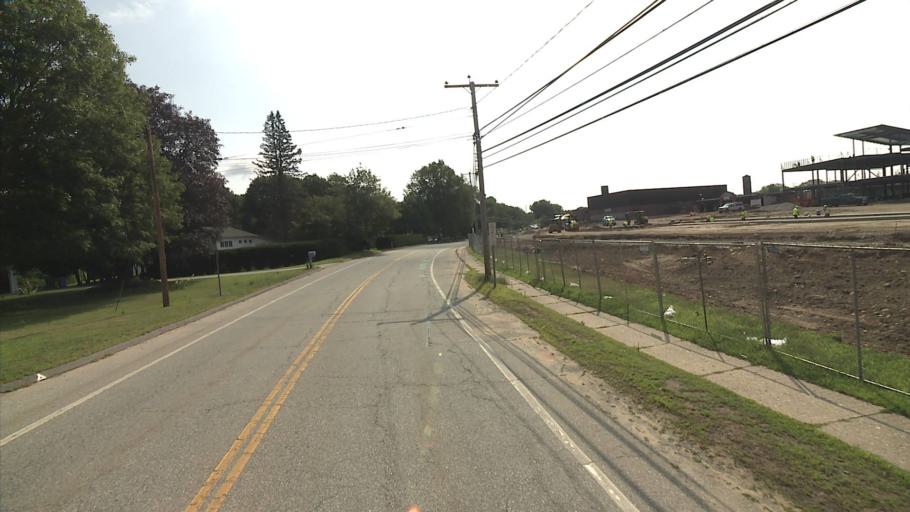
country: US
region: Connecticut
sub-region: New London County
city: Colchester
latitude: 41.5762
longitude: -72.3218
